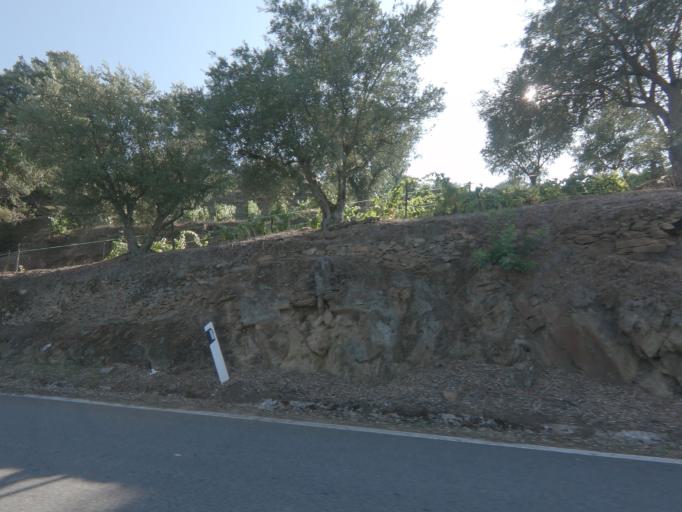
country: PT
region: Viseu
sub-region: Tabuaco
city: Tabuaco
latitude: 41.1399
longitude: -7.5638
